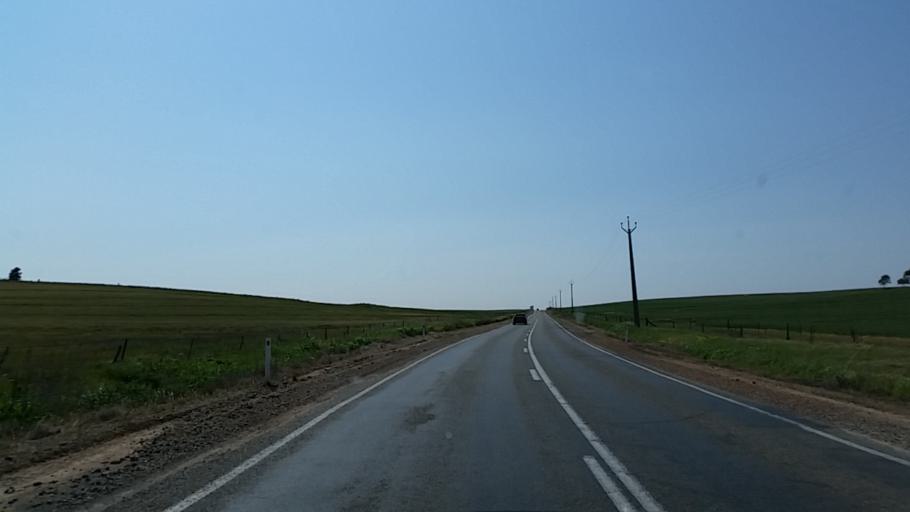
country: AU
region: South Australia
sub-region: Northern Areas
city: Jamestown
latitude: -33.1976
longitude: 138.4444
